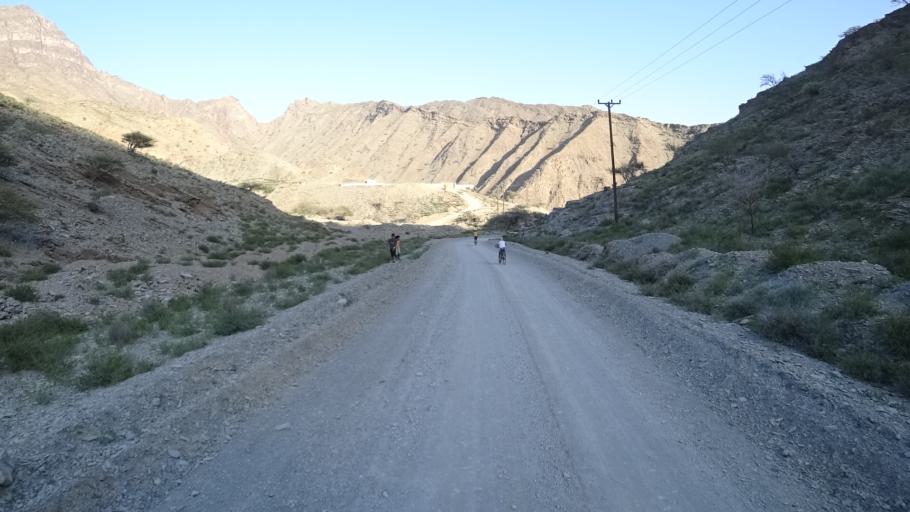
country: OM
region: Al Batinah
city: Rustaq
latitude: 23.2673
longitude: 57.3941
